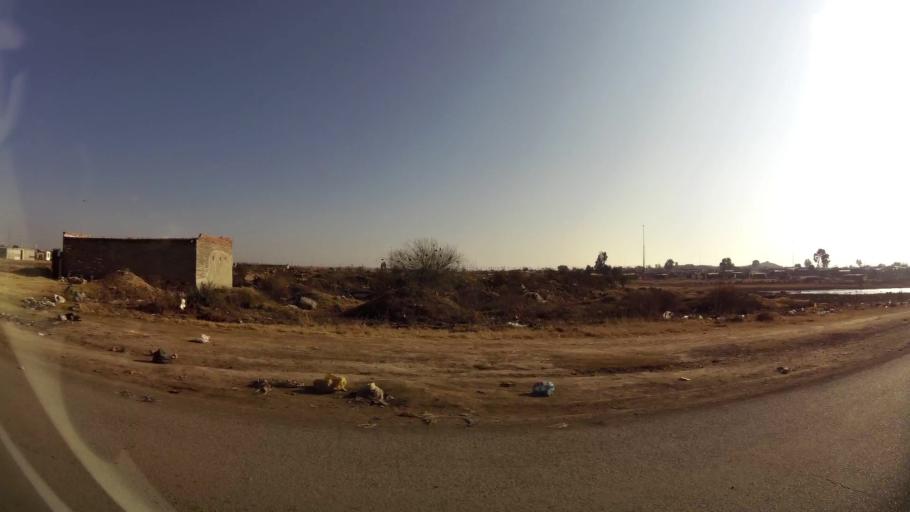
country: ZA
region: Orange Free State
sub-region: Mangaung Metropolitan Municipality
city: Bloemfontein
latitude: -29.1971
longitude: 26.2629
